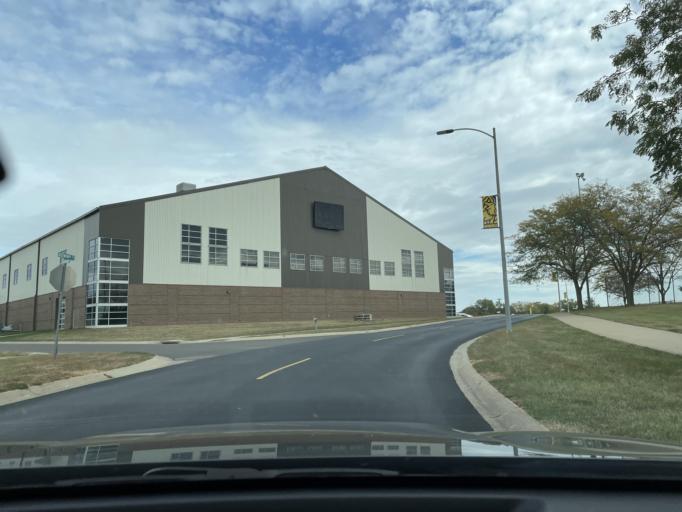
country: US
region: Missouri
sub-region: Buchanan County
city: Saint Joseph
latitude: 39.7608
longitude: -94.7893
